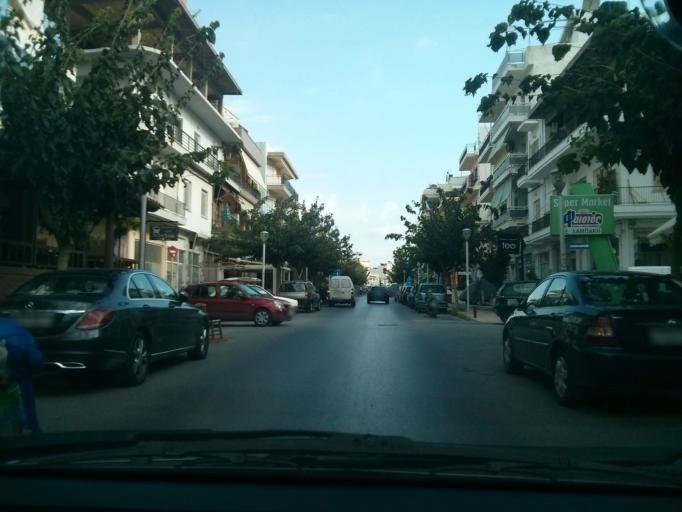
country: GR
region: Crete
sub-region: Nomos Irakleiou
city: Irakleion
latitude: 35.3299
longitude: 25.1366
